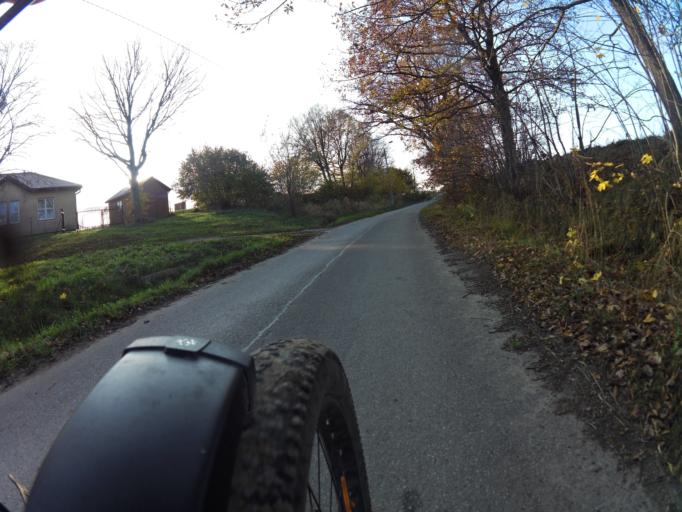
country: PL
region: Pomeranian Voivodeship
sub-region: Powiat pucki
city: Krokowa
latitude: 54.7513
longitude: 18.1858
